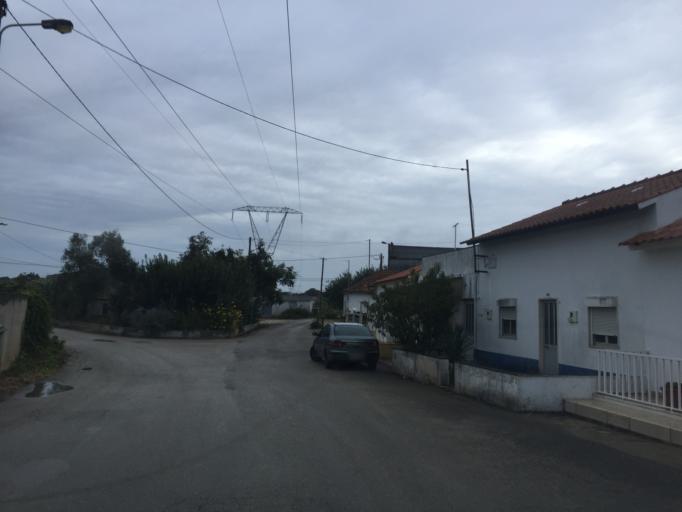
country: PT
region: Leiria
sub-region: Alcobaca
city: Benedita
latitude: 39.4327
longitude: -8.9534
